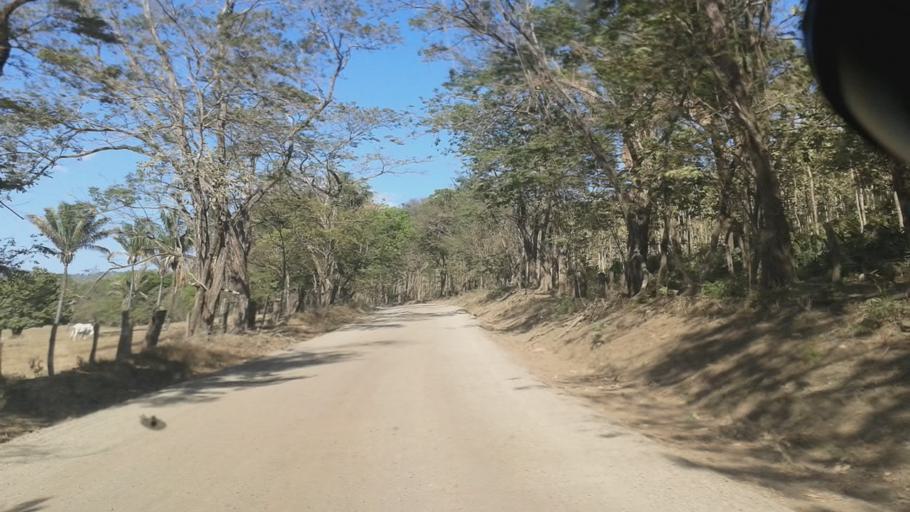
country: CR
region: Guanacaste
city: Samara
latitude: 9.9015
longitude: -85.5853
